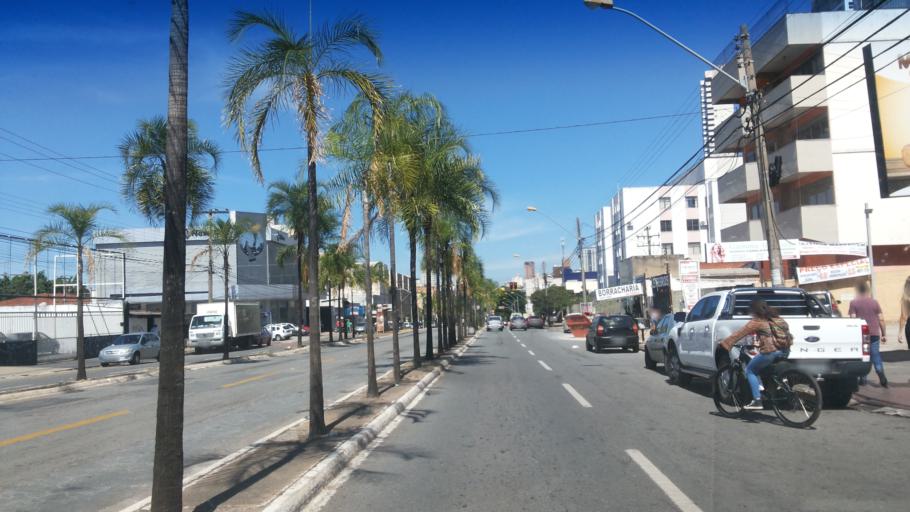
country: BR
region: Goias
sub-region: Goiania
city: Goiania
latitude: -16.6994
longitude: -49.2527
